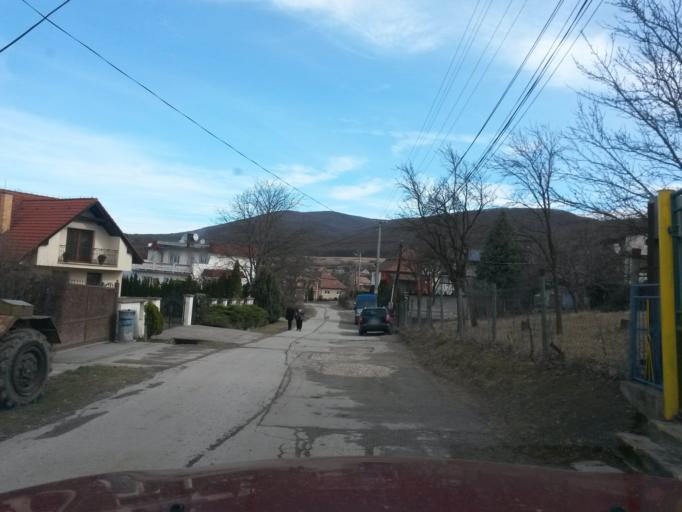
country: HU
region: Borsod-Abauj-Zemplen
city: Gonc
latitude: 48.5872
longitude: 21.3725
